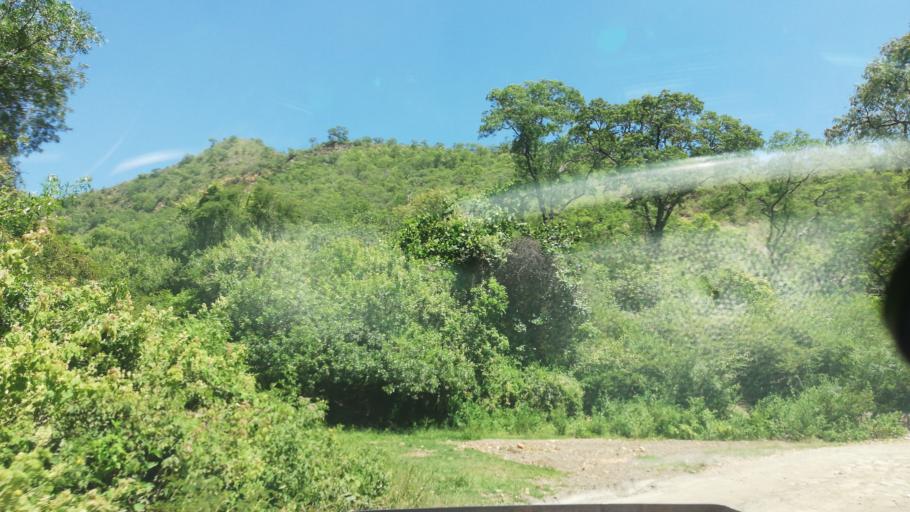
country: BO
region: Cochabamba
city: Mizque
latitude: -17.8852
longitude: -65.2869
